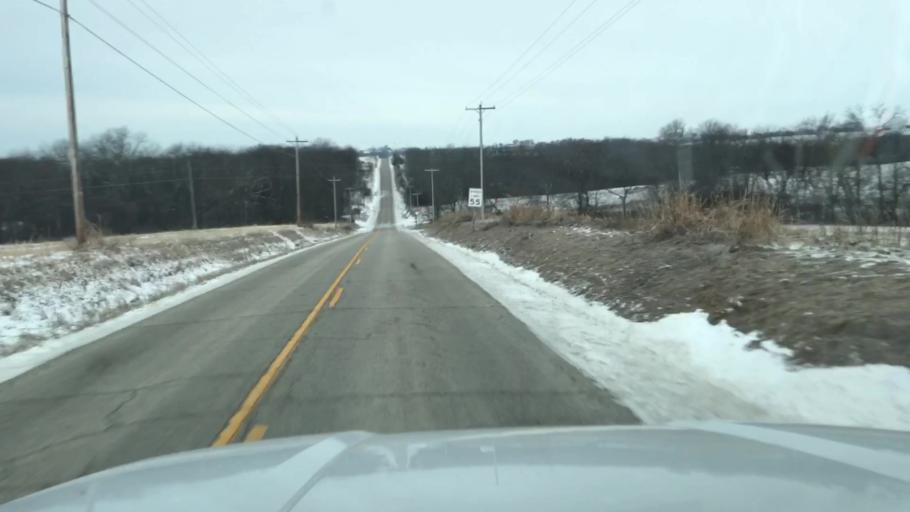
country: US
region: Missouri
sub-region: Andrew County
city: Savannah
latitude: 40.0247
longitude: -94.8875
